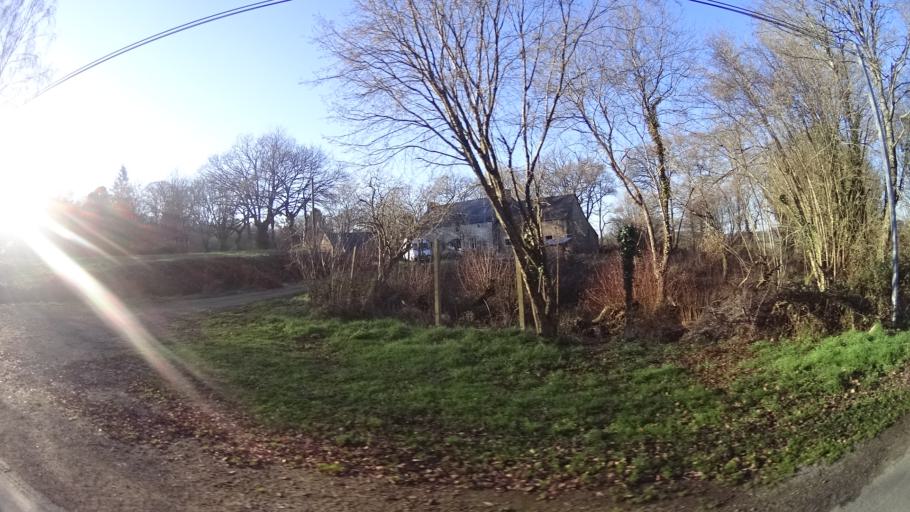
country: FR
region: Brittany
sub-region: Departement du Morbihan
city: Saint-Jacut-les-Pins
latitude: 47.6722
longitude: -2.2040
